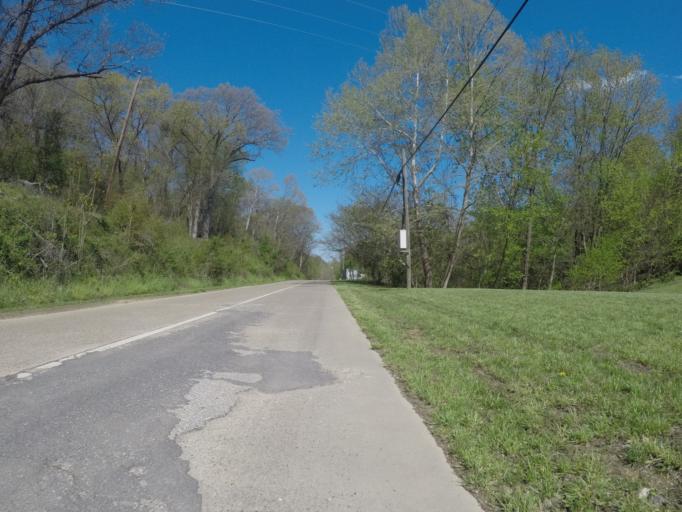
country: US
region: West Virginia
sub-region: Wayne County
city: Kenova
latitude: 38.3890
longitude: -82.5803
